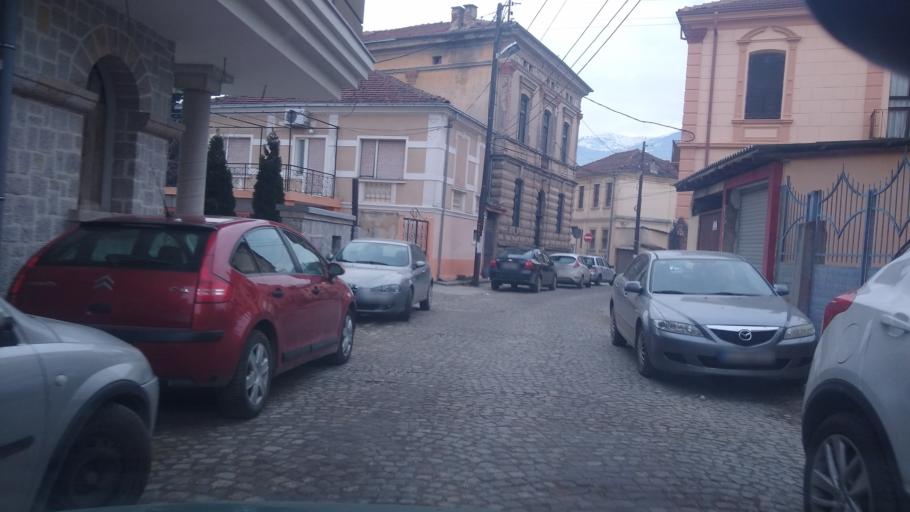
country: MK
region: Bitola
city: Bitola
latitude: 41.0300
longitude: 21.3333
